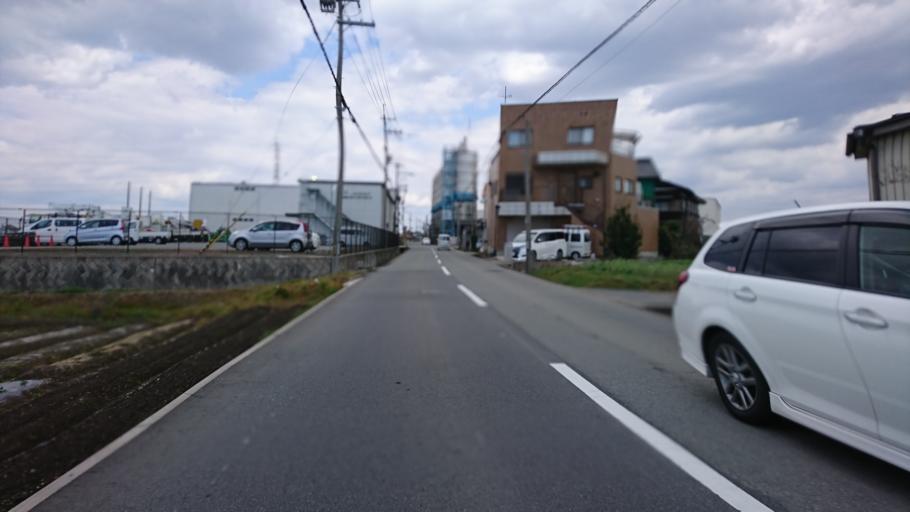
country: JP
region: Hyogo
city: Miki
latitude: 34.7401
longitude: 134.9298
